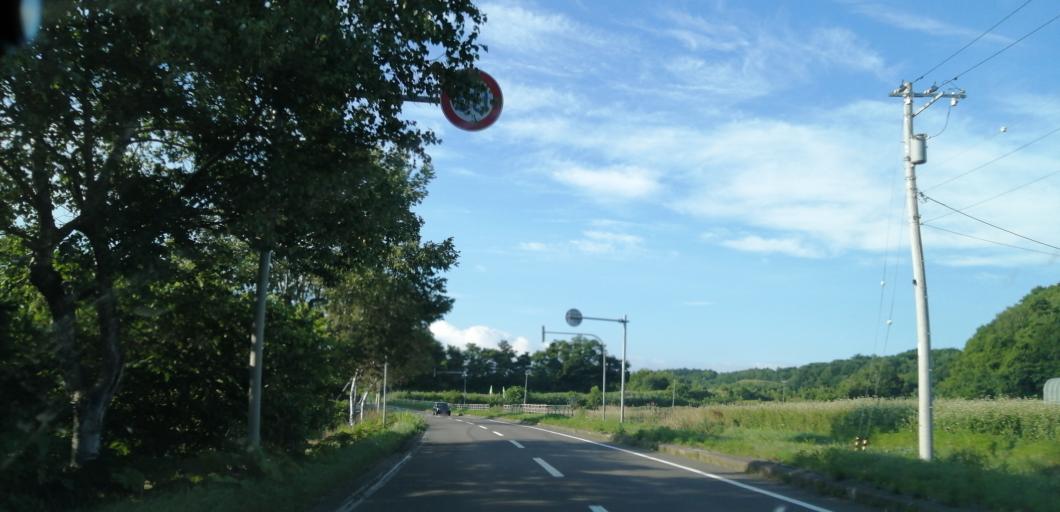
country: JP
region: Hokkaido
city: Chitose
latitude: 42.9141
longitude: 141.7275
